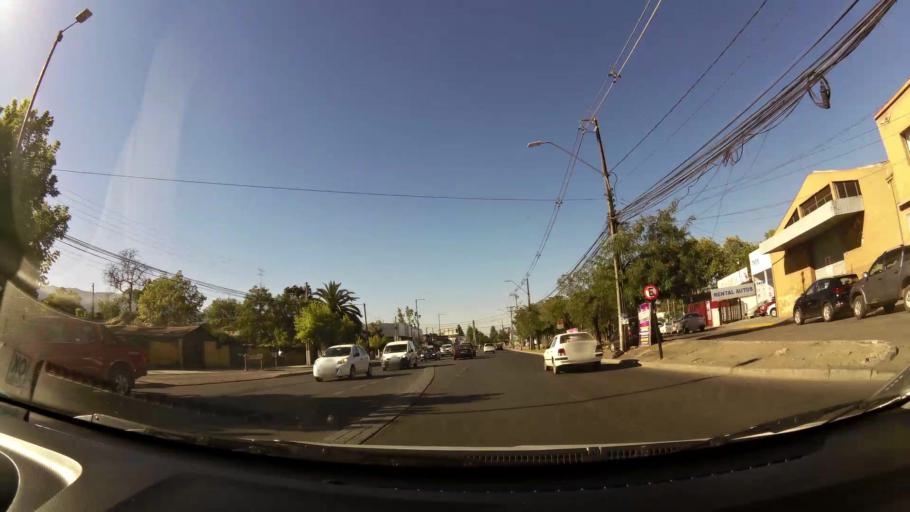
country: CL
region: O'Higgins
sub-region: Provincia de Colchagua
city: Chimbarongo
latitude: -34.5856
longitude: -70.9845
